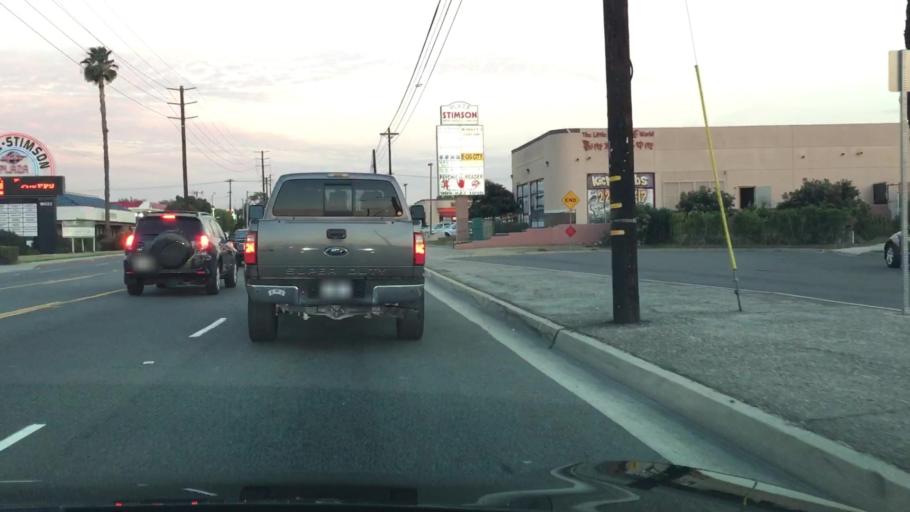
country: US
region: California
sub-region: Los Angeles County
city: La Puente
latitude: 34.0092
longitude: -117.9579
